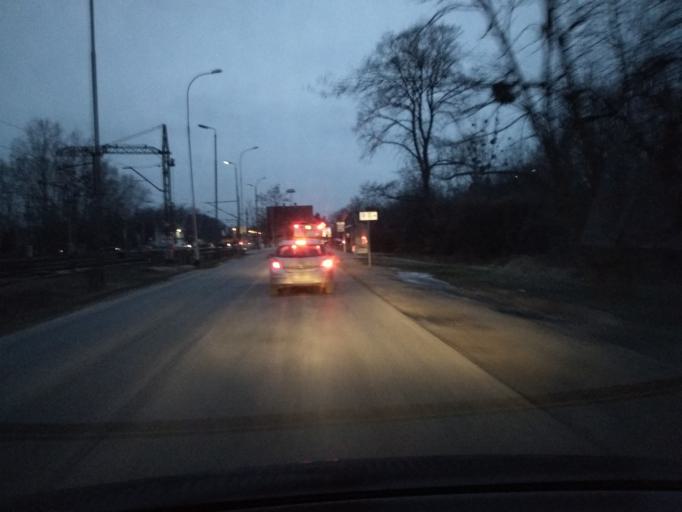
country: PL
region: Lower Silesian Voivodeship
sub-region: Powiat wroclawski
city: Wroclaw
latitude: 51.1259
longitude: 16.9555
